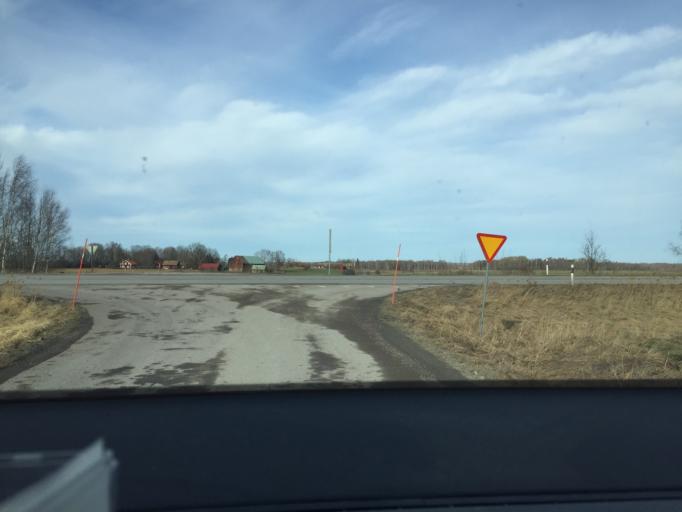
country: SE
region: OErebro
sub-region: Hallsbergs Kommun
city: Skollersta
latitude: 59.1485
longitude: 15.4125
